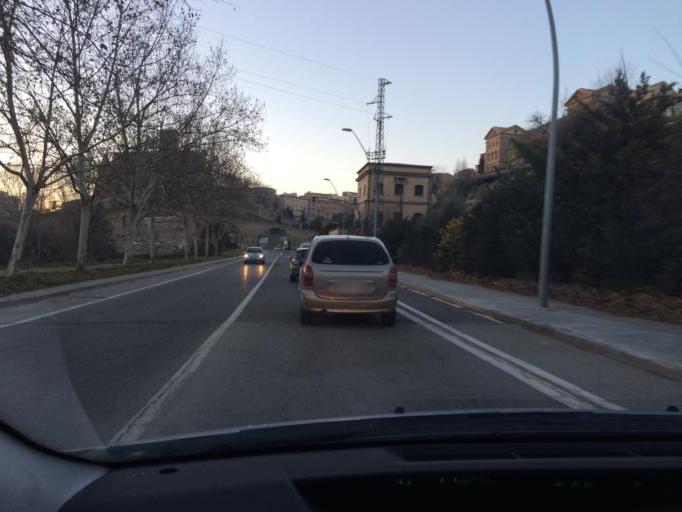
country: ES
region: Catalonia
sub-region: Provincia de Barcelona
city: Manresa
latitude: 41.7198
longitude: 1.8318
